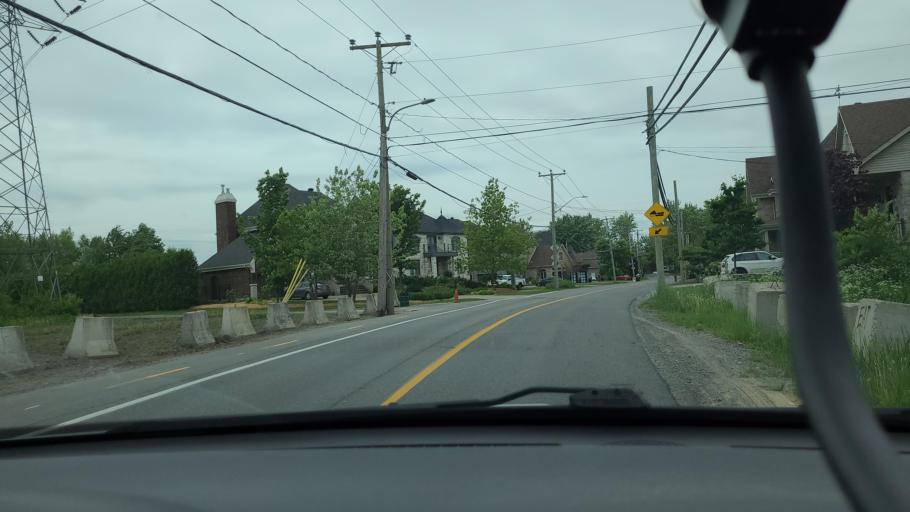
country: CA
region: Quebec
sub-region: Laurentides
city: Rosemere
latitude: 45.6345
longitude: -73.7652
